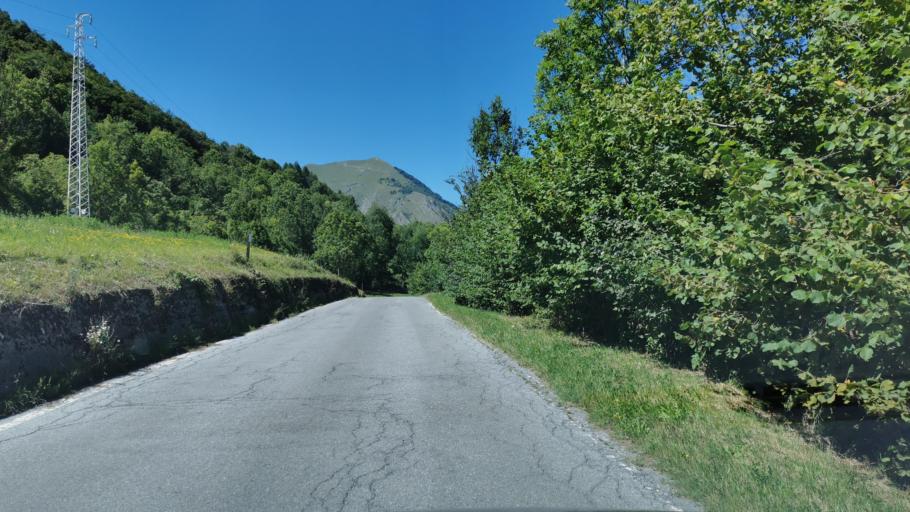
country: IT
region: Piedmont
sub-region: Provincia di Cuneo
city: Entracque
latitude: 44.2390
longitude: 7.3911
